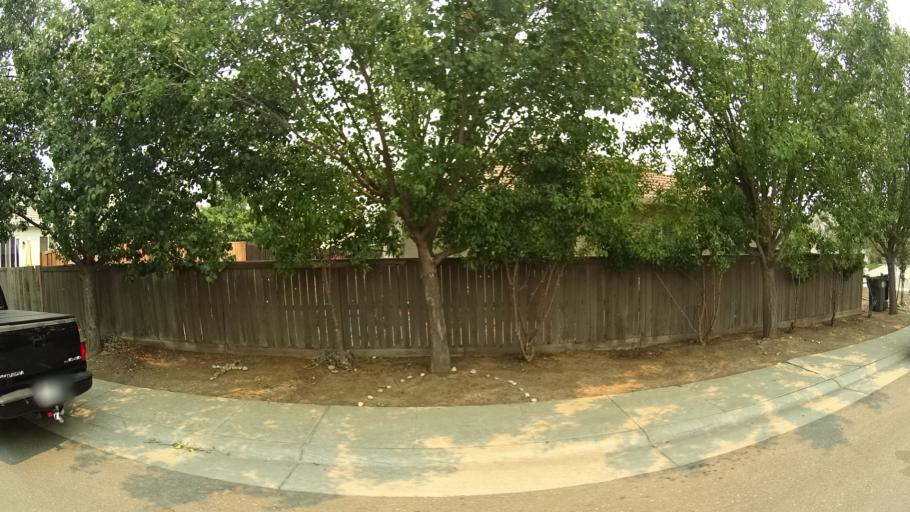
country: US
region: California
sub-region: Sacramento County
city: Laguna
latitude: 38.4029
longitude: -121.4209
